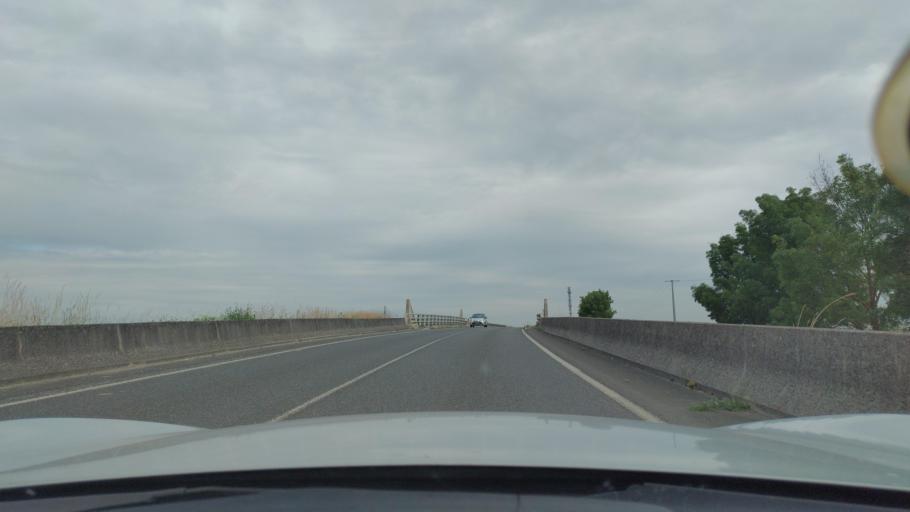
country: FR
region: Ile-de-France
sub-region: Departement de Seine-et-Marne
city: Cregy-les-Meaux
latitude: 49.0081
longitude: 2.8795
